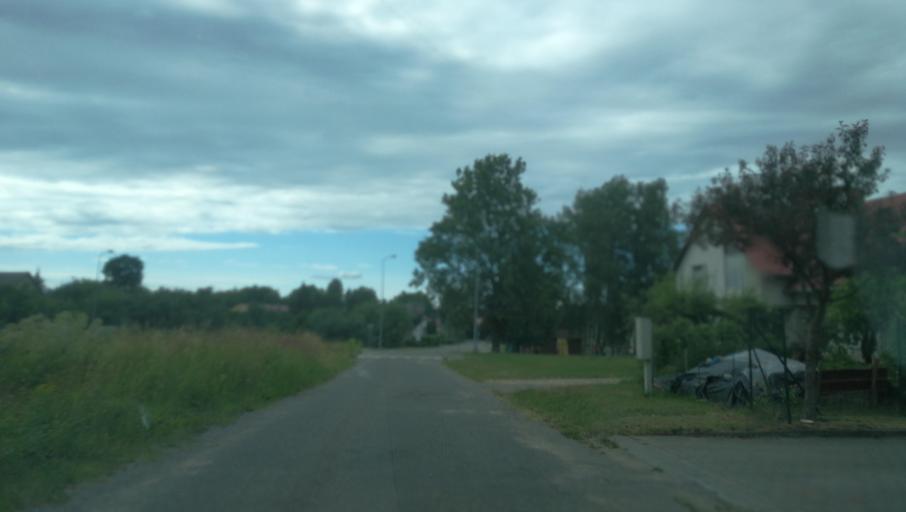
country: LV
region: Cesu Rajons
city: Cesis
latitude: 57.3044
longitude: 25.2841
